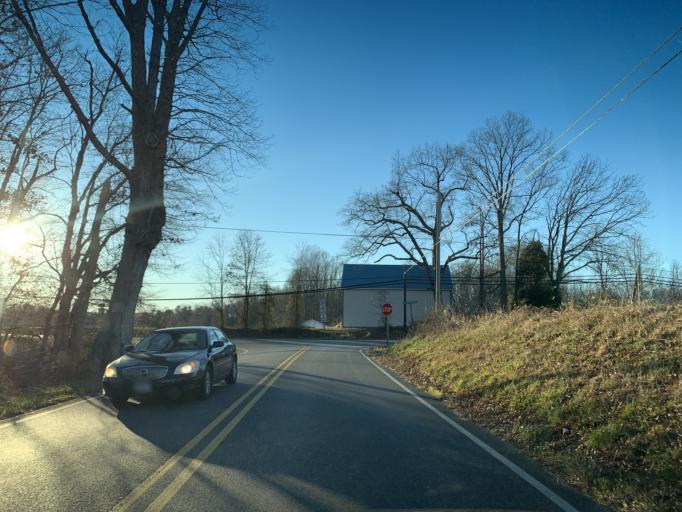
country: US
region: Maryland
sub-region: Saint Mary's County
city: Mechanicsville
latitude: 38.4687
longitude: -76.7299
